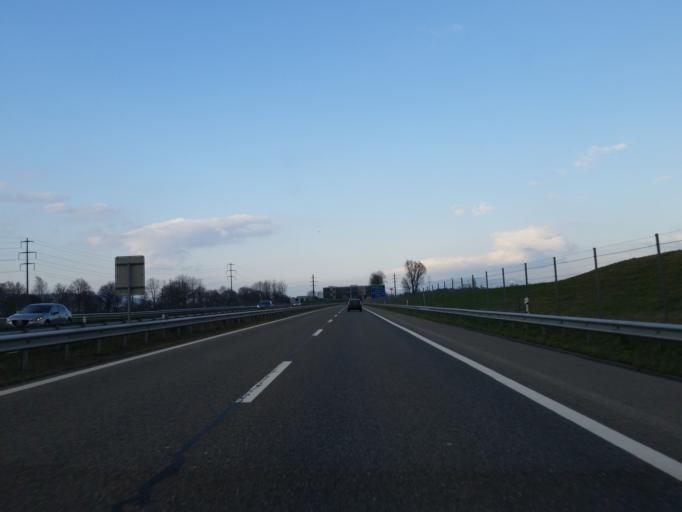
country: AT
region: Vorarlberg
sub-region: Politischer Bezirk Feldkirch
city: Mader
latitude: 47.3508
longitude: 9.6009
